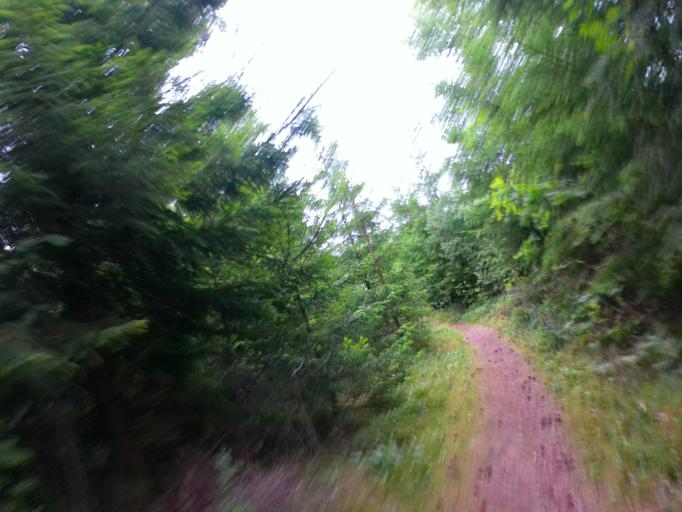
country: SE
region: Vaestra Goetaland
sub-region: Vargarda Kommun
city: Jonstorp
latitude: 58.0317
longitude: 12.6089
